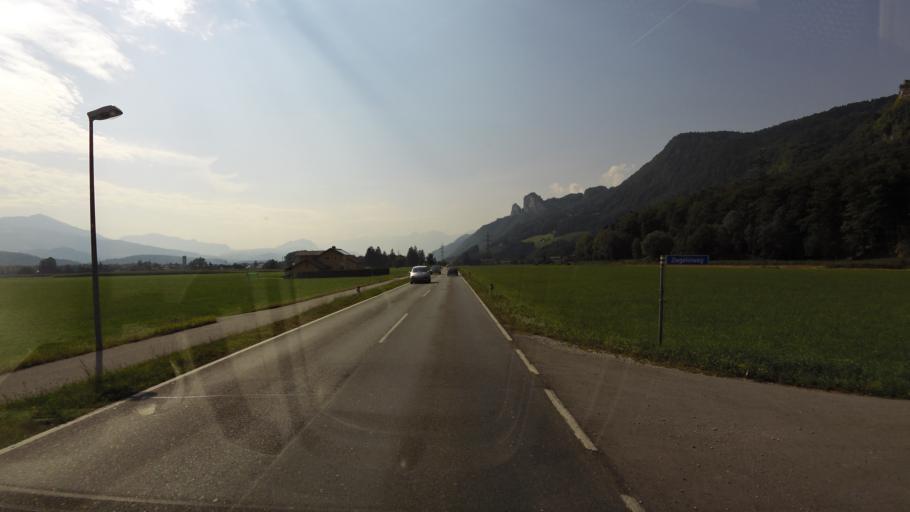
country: DE
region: Bavaria
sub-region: Upper Bavaria
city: Marktschellenberg
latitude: 47.7139
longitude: 13.0633
